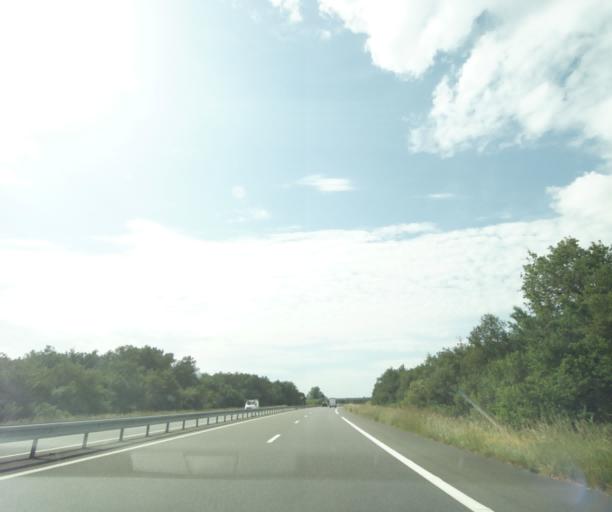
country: FR
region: Pays de la Loire
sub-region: Departement de Maine-et-Loire
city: Maze
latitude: 47.4912
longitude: -0.2692
